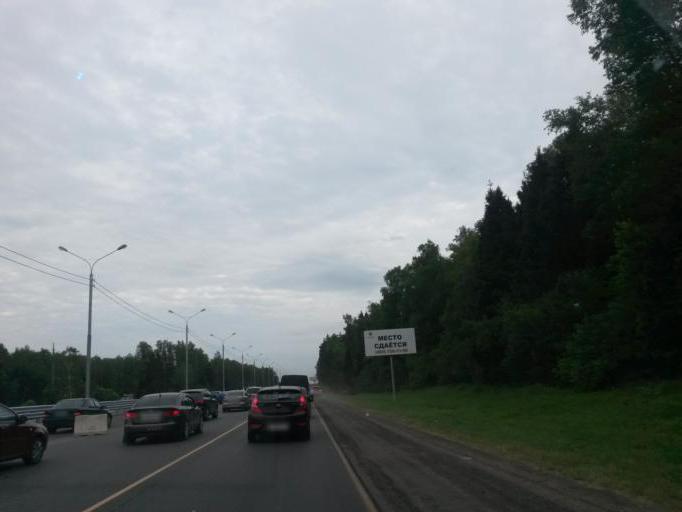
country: RU
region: Moskovskaya
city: Lyubuchany
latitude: 55.2669
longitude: 37.5358
